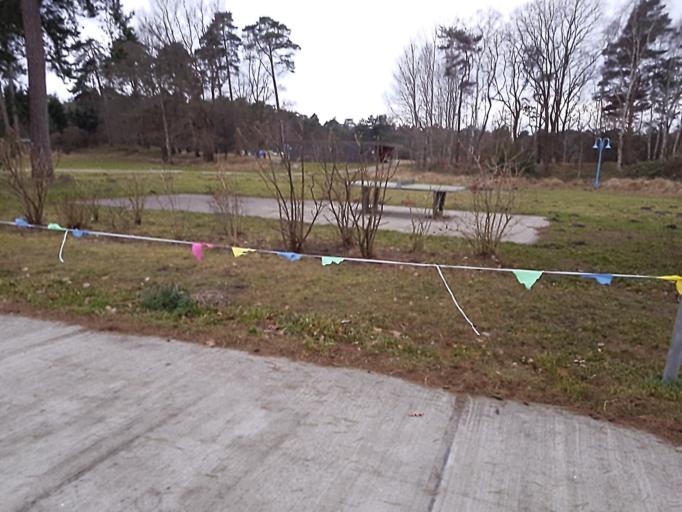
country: DE
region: Mecklenburg-Vorpommern
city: Ostseebad Binz
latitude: 54.4512
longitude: 13.5693
